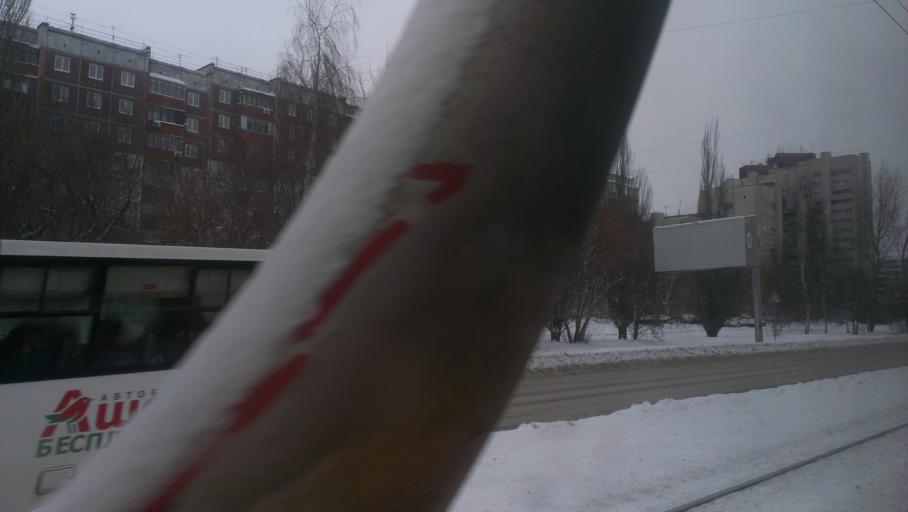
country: RU
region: Altai Krai
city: Novosilikatnyy
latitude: 53.3591
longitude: 83.6748
